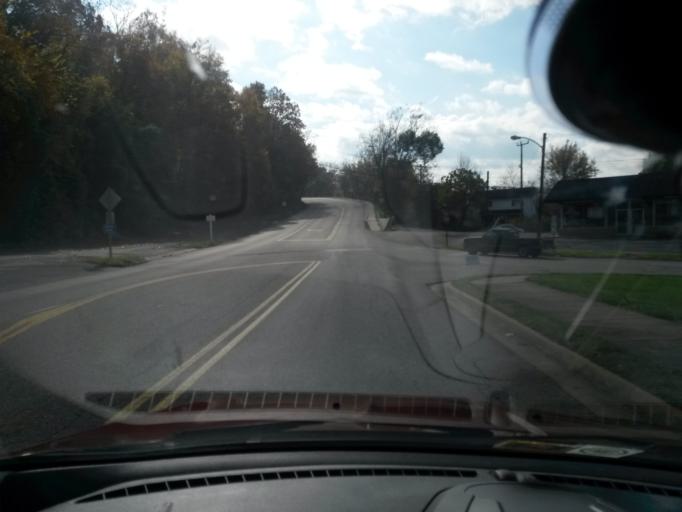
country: US
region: Virginia
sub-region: City of Covington
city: Fairlawn
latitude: 37.7813
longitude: -79.9863
